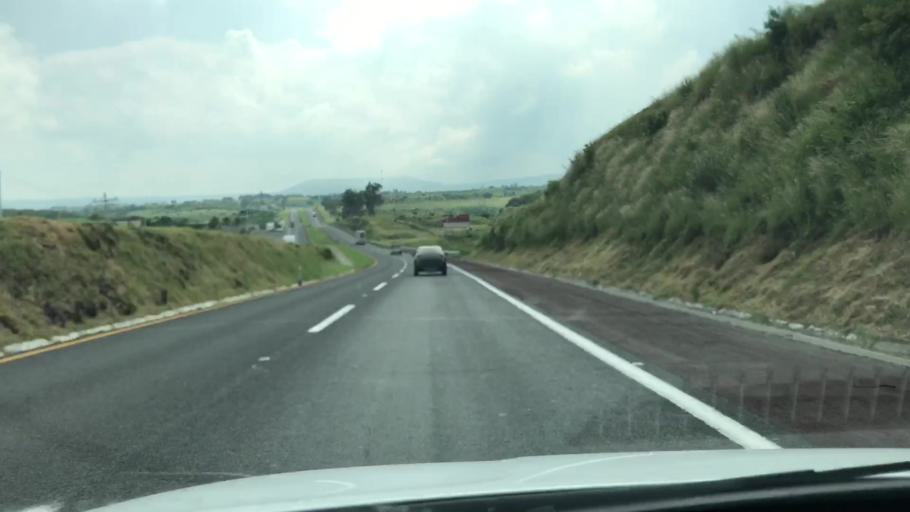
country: MX
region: Jalisco
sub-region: Tonala
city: Mismaloya (Fraccionamiento Pedregal de Santa Martha)
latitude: 20.6083
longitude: -103.1231
